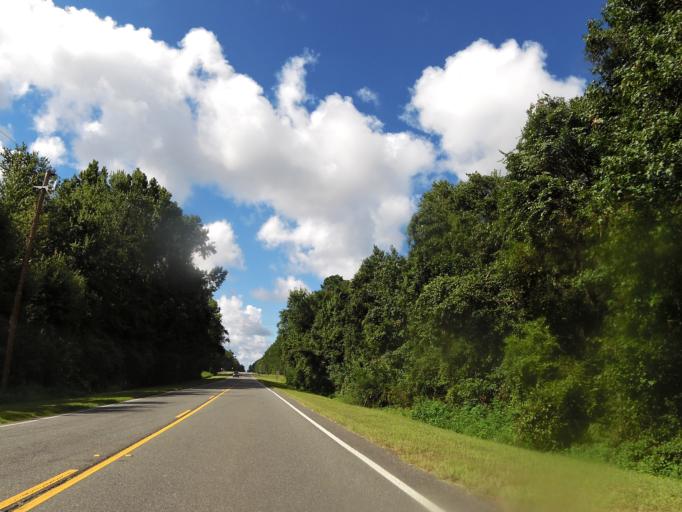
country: US
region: Georgia
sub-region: Camden County
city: Kingsland
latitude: 30.7831
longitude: -81.6868
